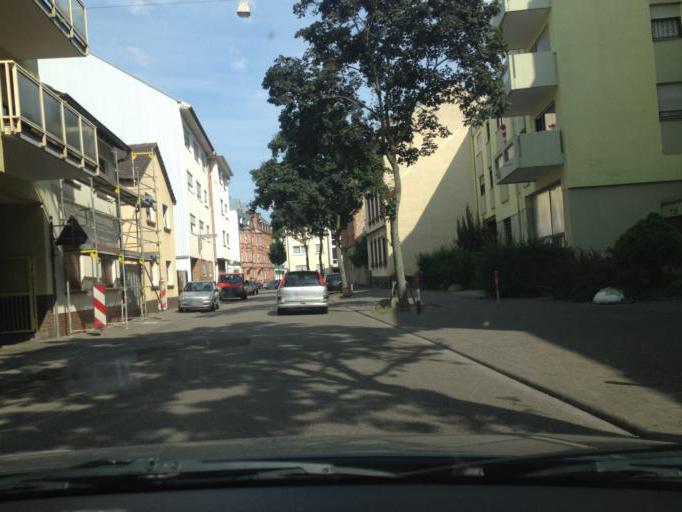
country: DE
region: Rheinland-Pfalz
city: Altrip
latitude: 49.4545
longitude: 8.4904
